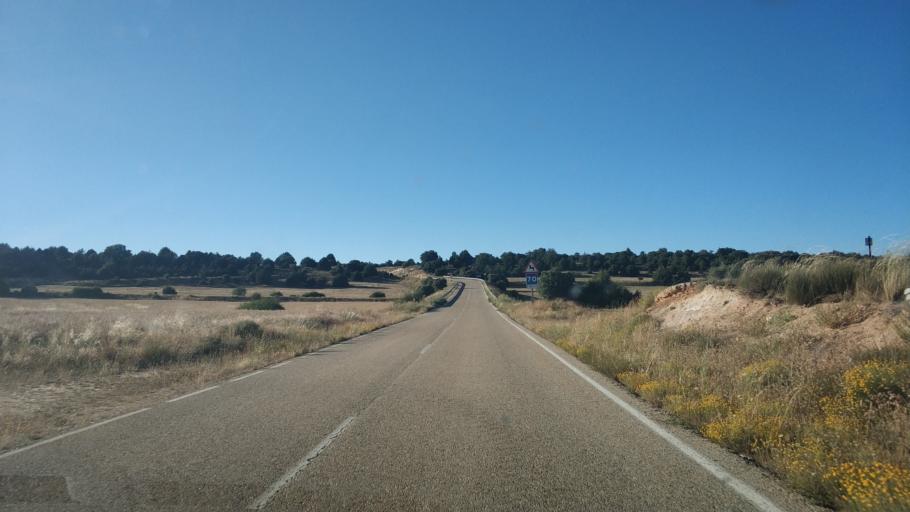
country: ES
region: Castille and Leon
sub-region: Provincia de Soria
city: Montejo de Tiermes
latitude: 41.3986
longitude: -3.1991
